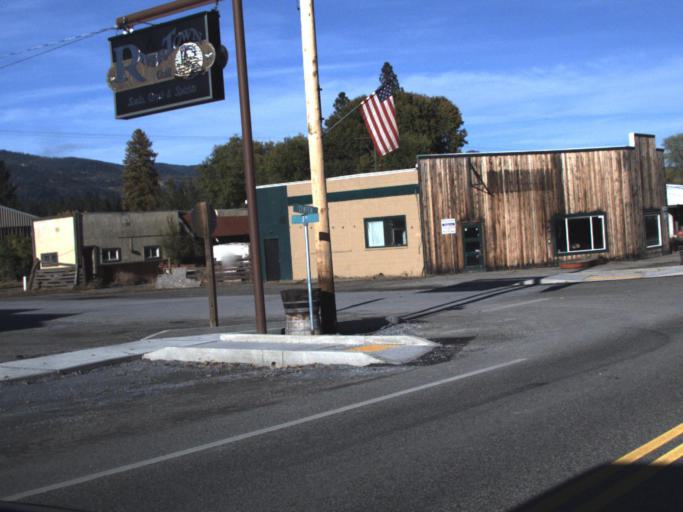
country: CA
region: British Columbia
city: Rossland
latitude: 48.9166
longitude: -117.7804
